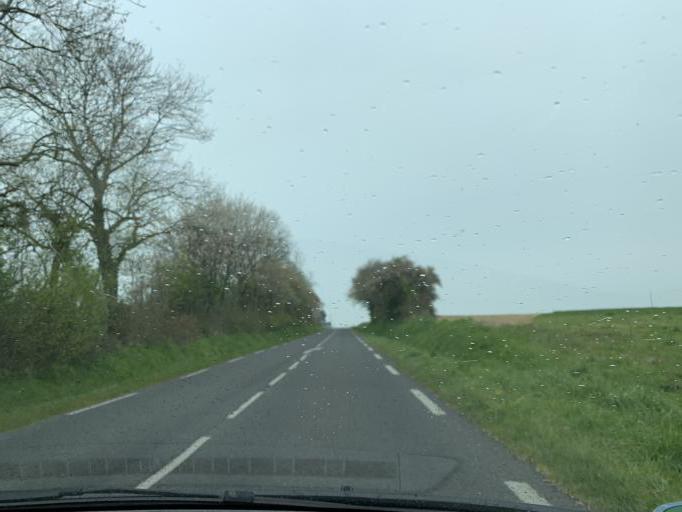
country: FR
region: Haute-Normandie
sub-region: Departement de la Seine-Maritime
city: Cany-Barville
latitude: 49.8075
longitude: 0.6677
